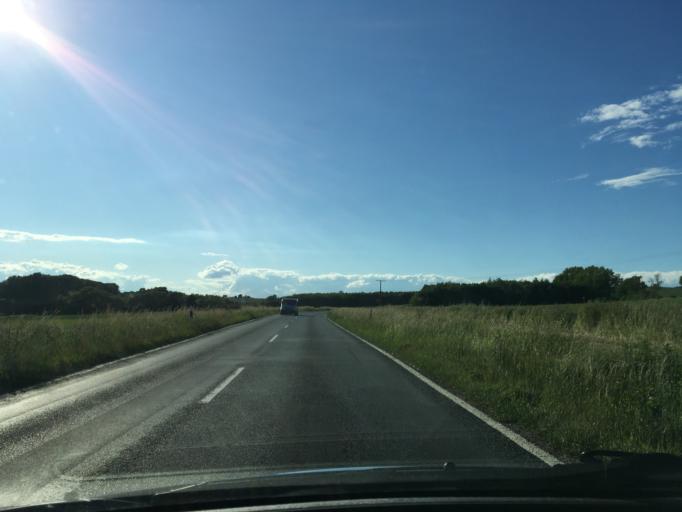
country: DE
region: Lower Saxony
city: Coppengrave
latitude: 51.9917
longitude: 9.7187
